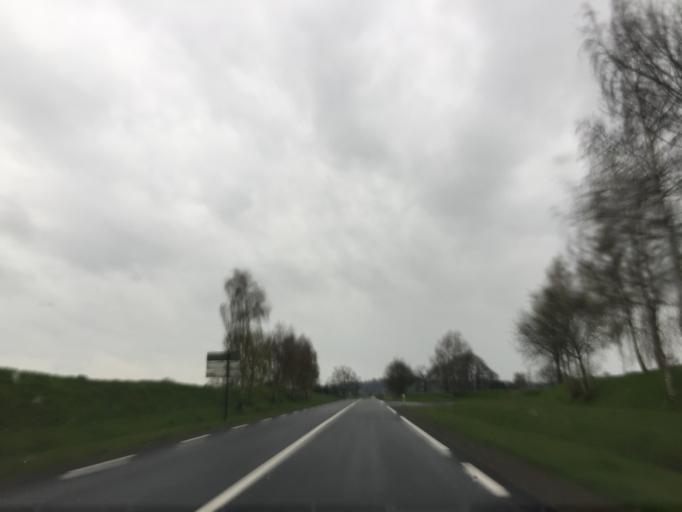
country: FR
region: Brittany
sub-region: Departement d'Ille-et-Vilaine
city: Beauce
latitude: 48.3149
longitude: -1.1820
